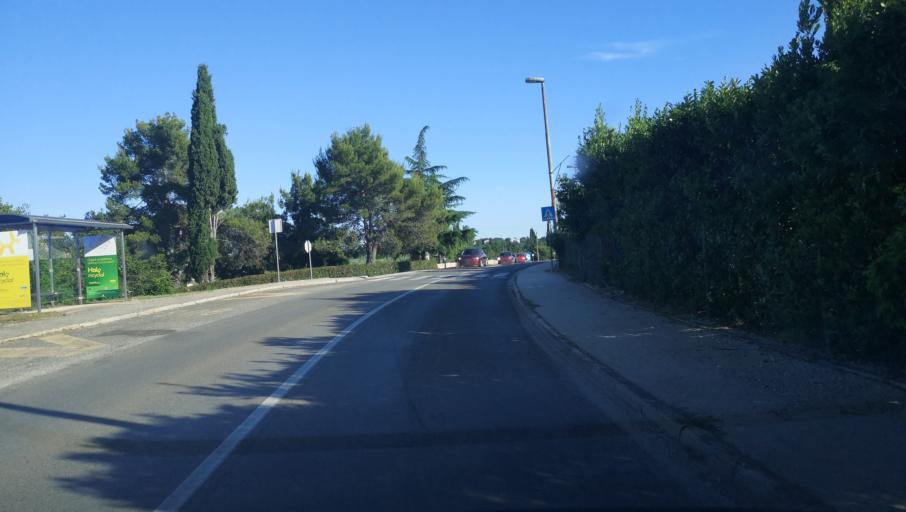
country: HR
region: Istarska
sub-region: Grad Rovinj
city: Rovinj
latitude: 45.0642
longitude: 13.6908
